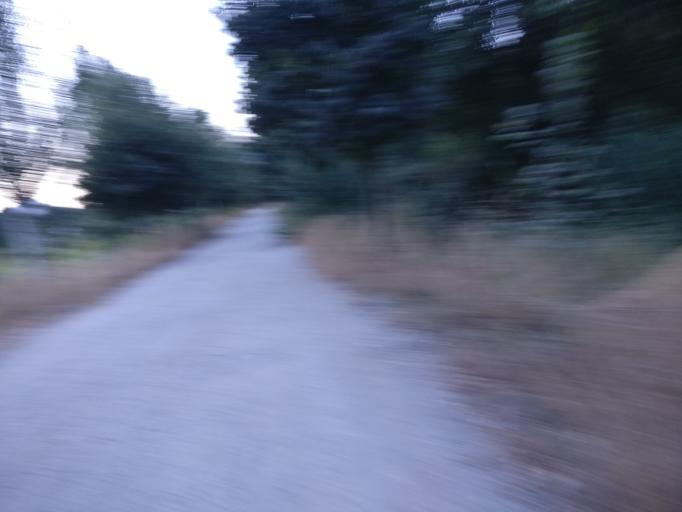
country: ES
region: Andalusia
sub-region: Provincia de Granada
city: Huetor Vega
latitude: 37.1603
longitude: -3.5573
